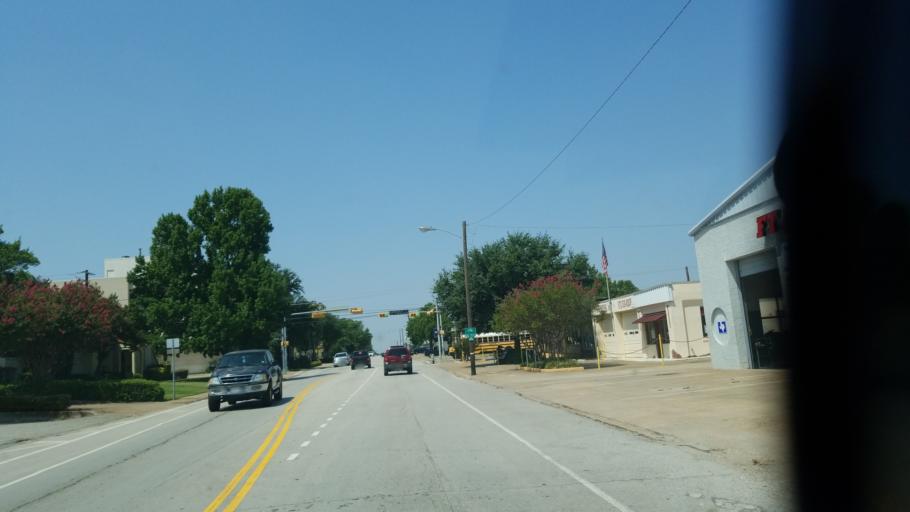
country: US
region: Texas
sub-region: Dallas County
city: Garland
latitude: 32.9127
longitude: -96.6393
